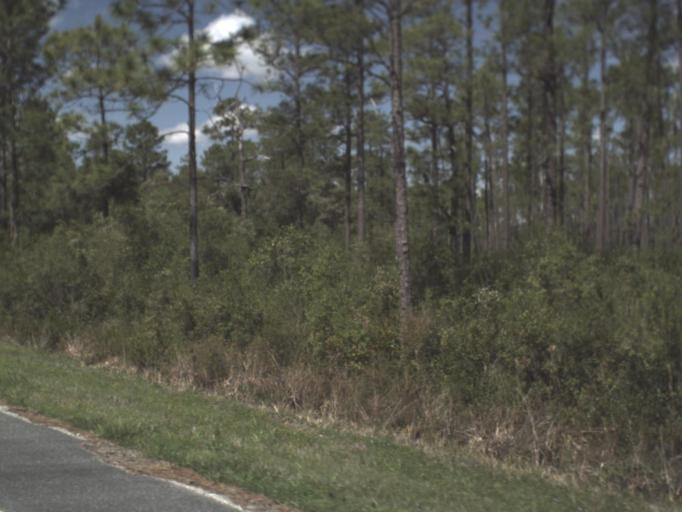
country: US
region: Florida
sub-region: Gadsden County
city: Midway
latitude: 30.3399
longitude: -84.4898
